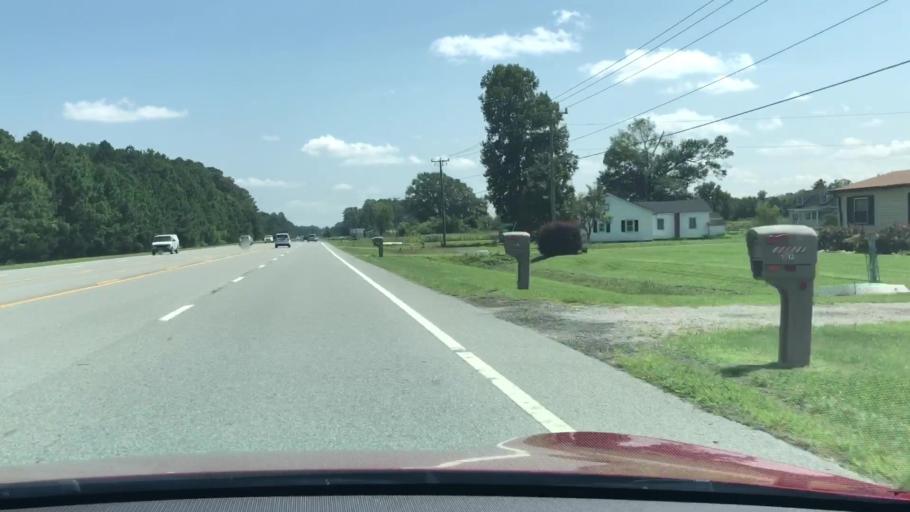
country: US
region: North Carolina
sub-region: Currituck County
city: Moyock
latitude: 36.4752
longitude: -76.1220
